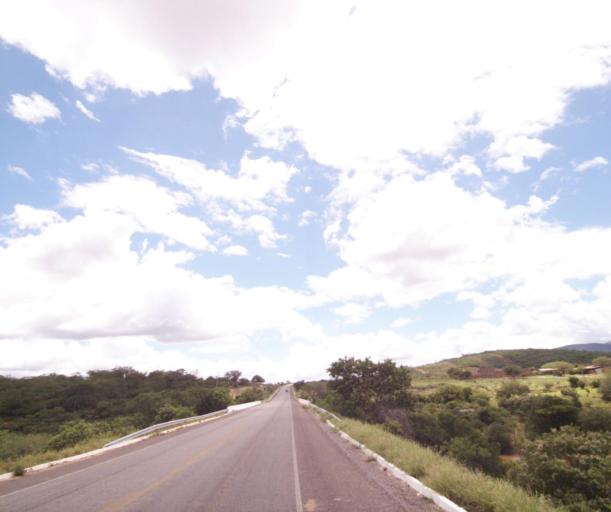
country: BR
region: Bahia
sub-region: Brumado
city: Brumado
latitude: -14.2320
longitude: -41.6818
